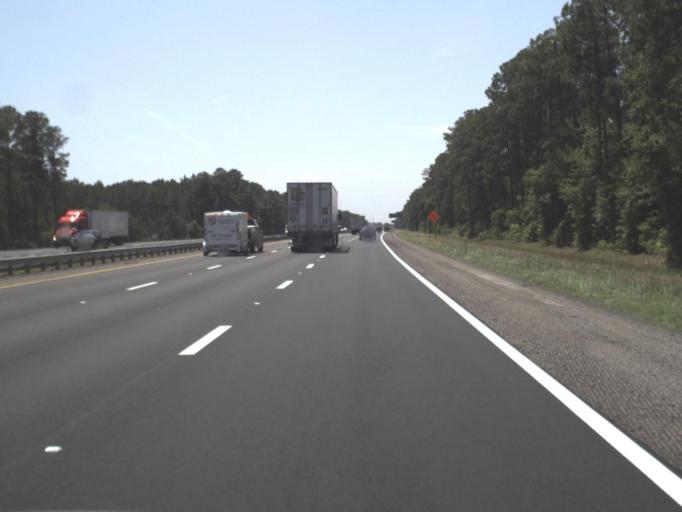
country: US
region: Florida
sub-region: Nassau County
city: Yulee
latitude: 30.5419
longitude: -81.6379
